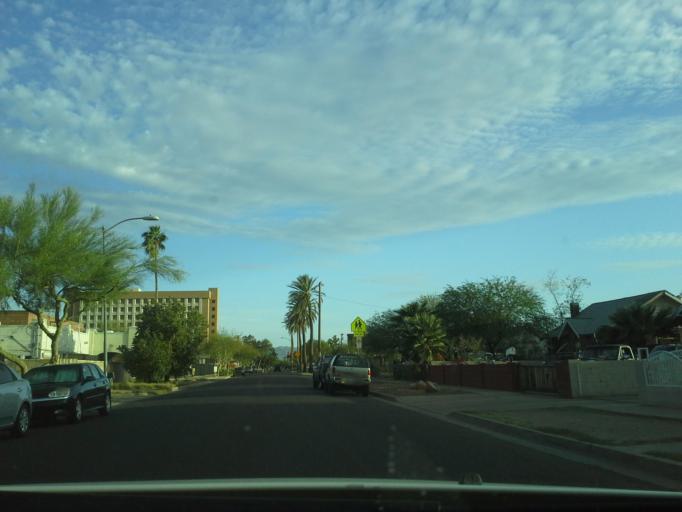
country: US
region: Arizona
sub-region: Maricopa County
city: Phoenix
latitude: 33.4539
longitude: -112.0957
